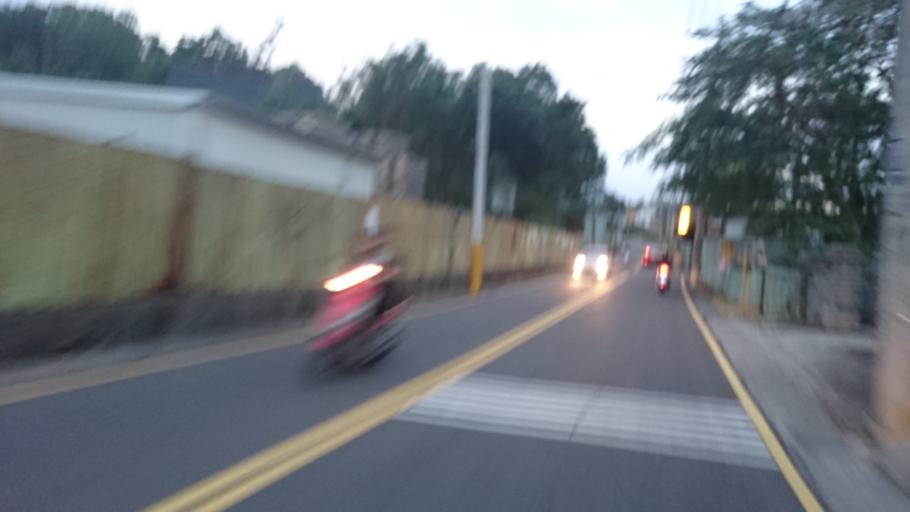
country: TW
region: Taiwan
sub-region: Hsinchu
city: Hsinchu
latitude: 24.7811
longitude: 120.9342
